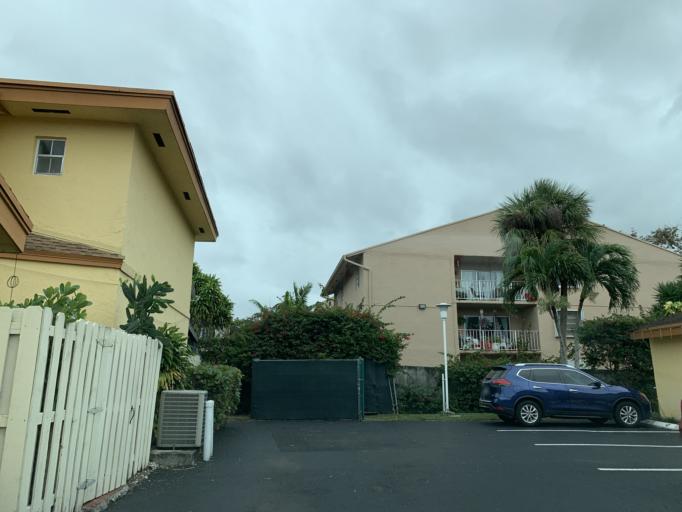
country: US
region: Florida
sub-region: Miami-Dade County
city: The Hammocks
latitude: 25.6883
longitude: -80.4436
